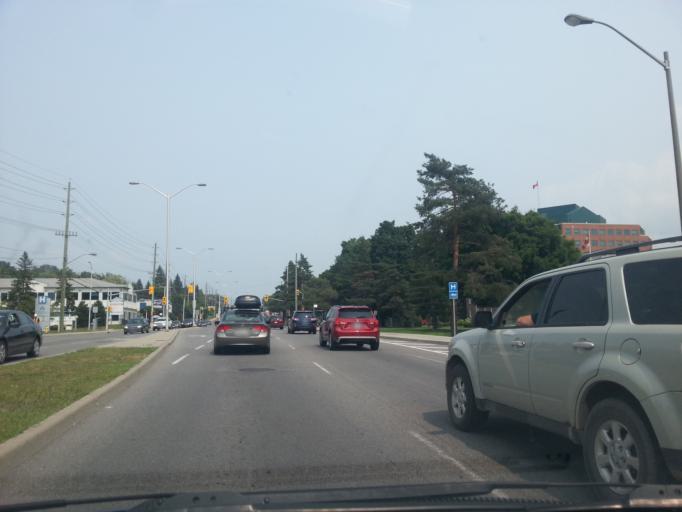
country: CA
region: Ontario
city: Ottawa
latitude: 45.4437
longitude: -75.6387
